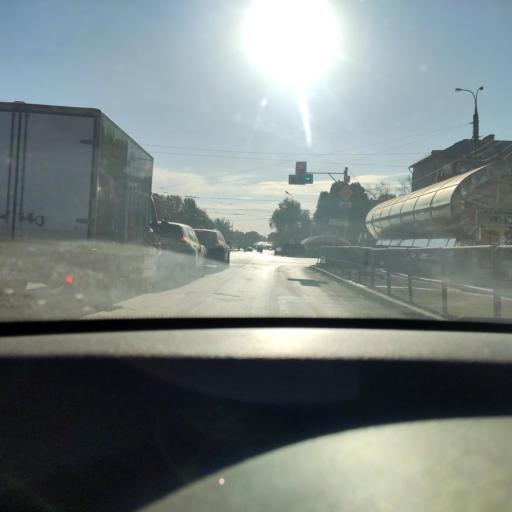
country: RU
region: Samara
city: Samara
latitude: 53.2071
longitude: 50.2343
